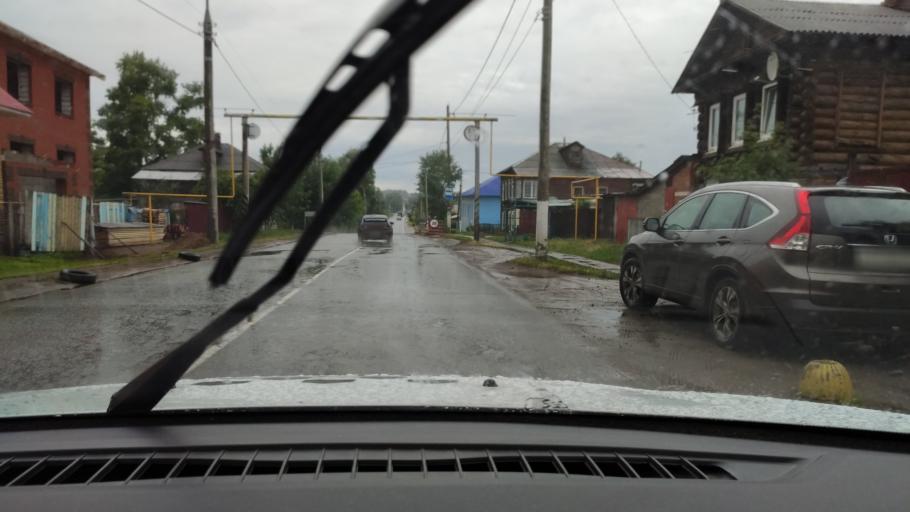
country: RU
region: Udmurtiya
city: Votkinsk
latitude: 57.0517
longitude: 53.9712
